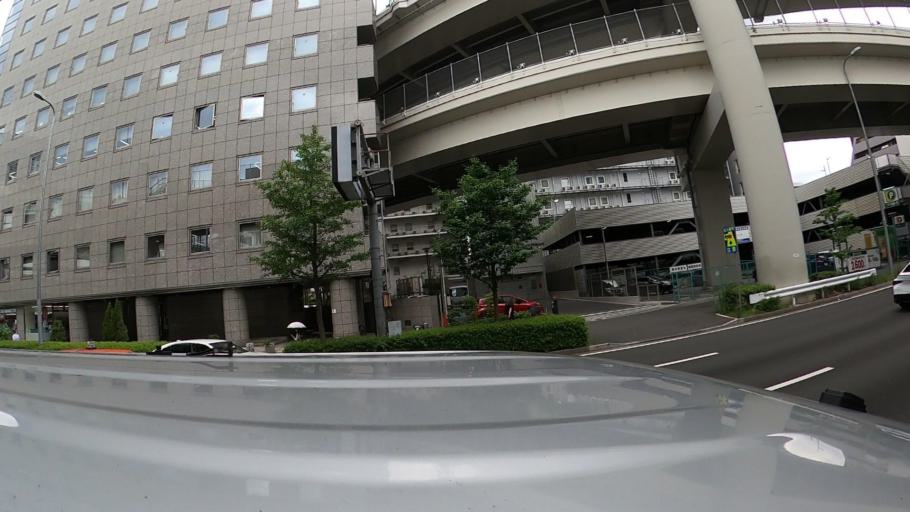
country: JP
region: Kanagawa
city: Yokohama
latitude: 35.4673
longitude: 139.6254
